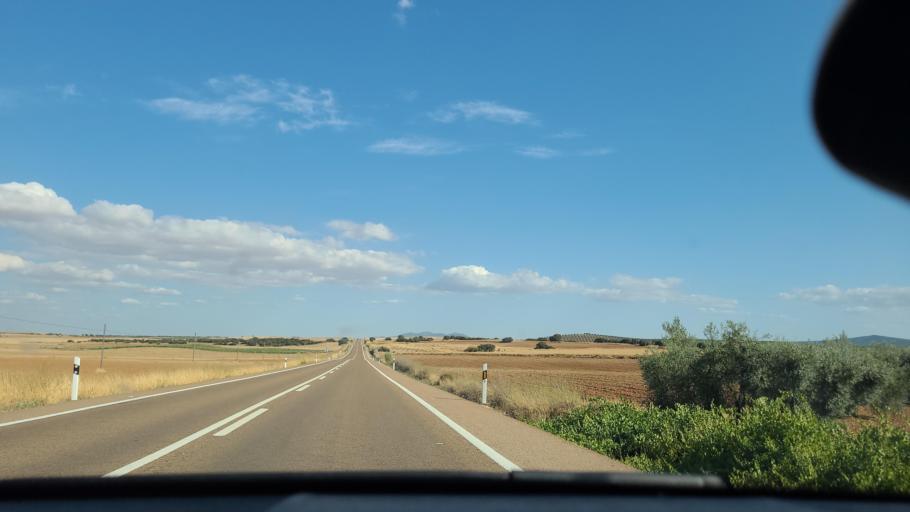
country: ES
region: Extremadura
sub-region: Provincia de Badajoz
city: Usagre
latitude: 38.3365
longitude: -6.1573
